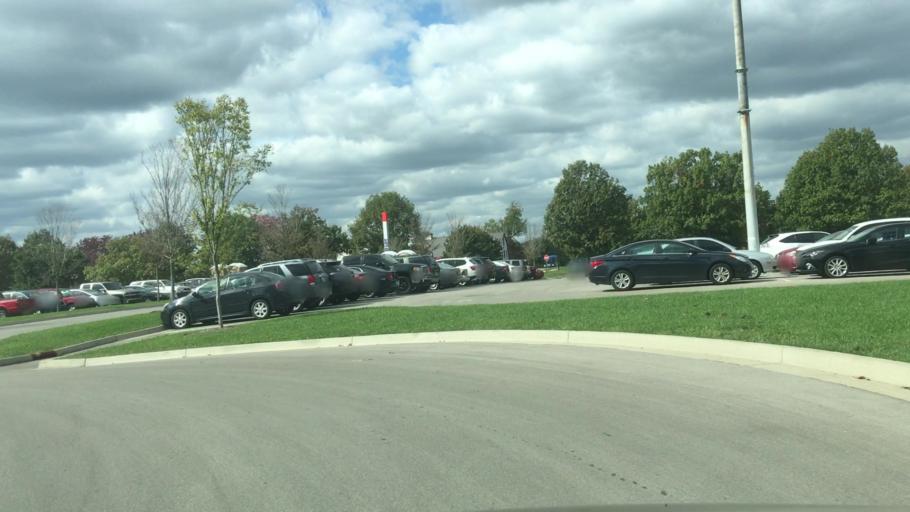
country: US
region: Kentucky
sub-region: Fayette County
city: Mount Vernon
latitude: 38.0243
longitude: -84.5057
